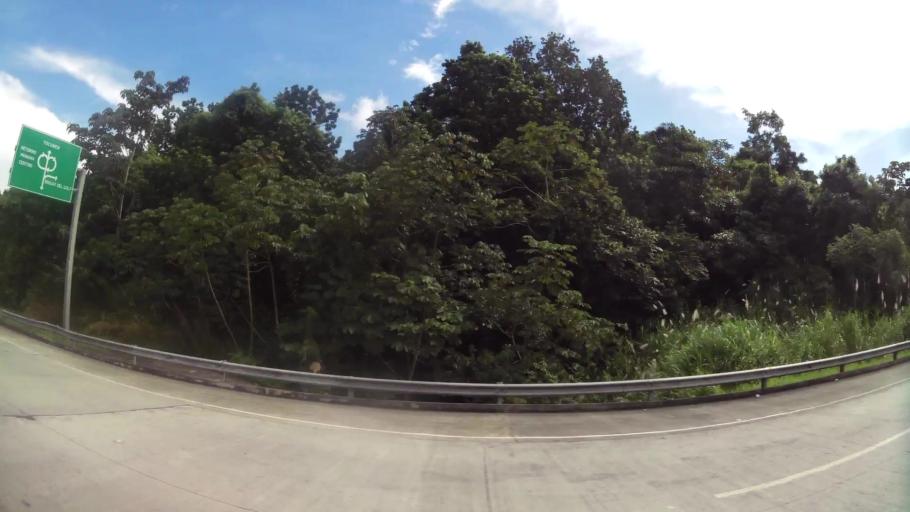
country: PA
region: Panama
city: San Miguelito
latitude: 9.0824
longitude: -79.4657
